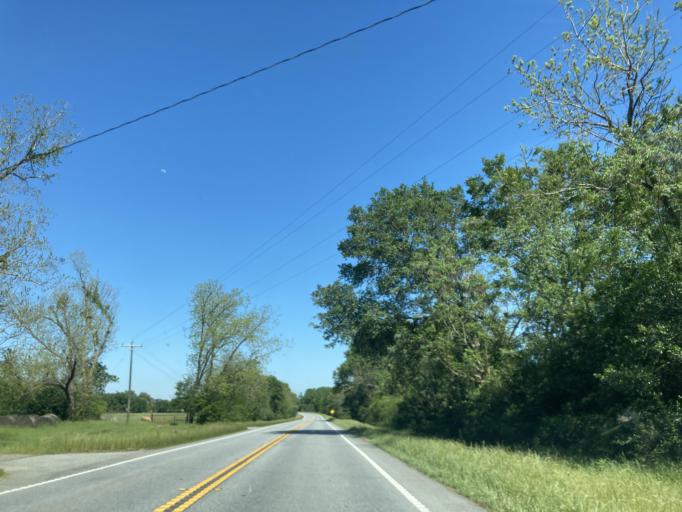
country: US
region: Georgia
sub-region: Miller County
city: Colquitt
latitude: 31.1834
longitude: -84.5459
